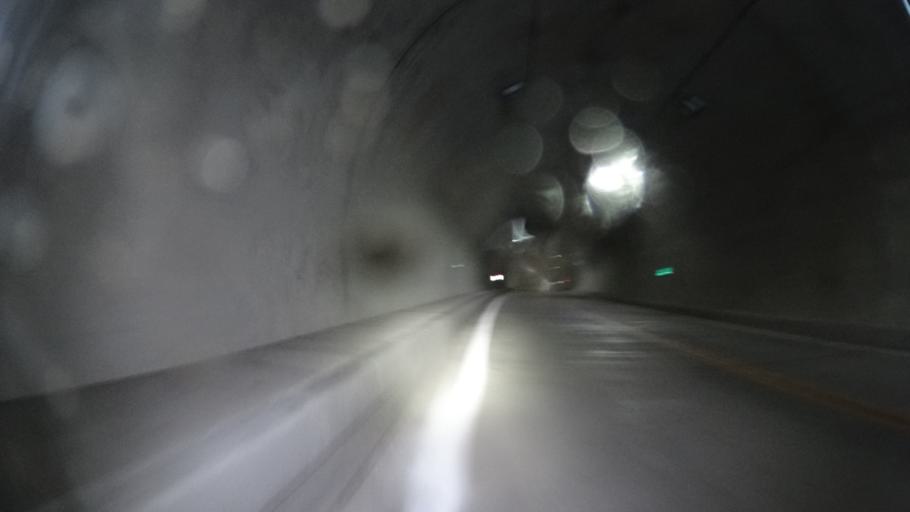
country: JP
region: Yamanashi
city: Enzan
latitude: 35.7999
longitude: 138.8652
